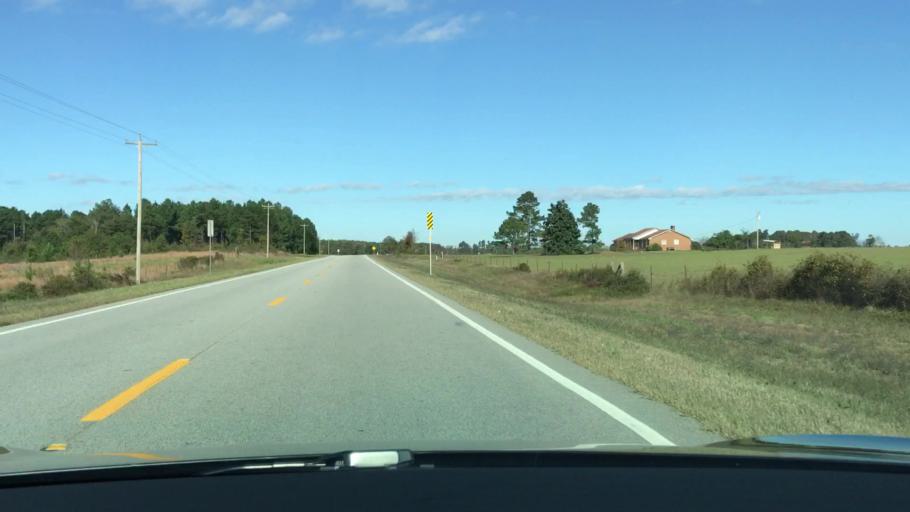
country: US
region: Georgia
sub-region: Glascock County
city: Gibson
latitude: 33.2910
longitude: -82.5099
